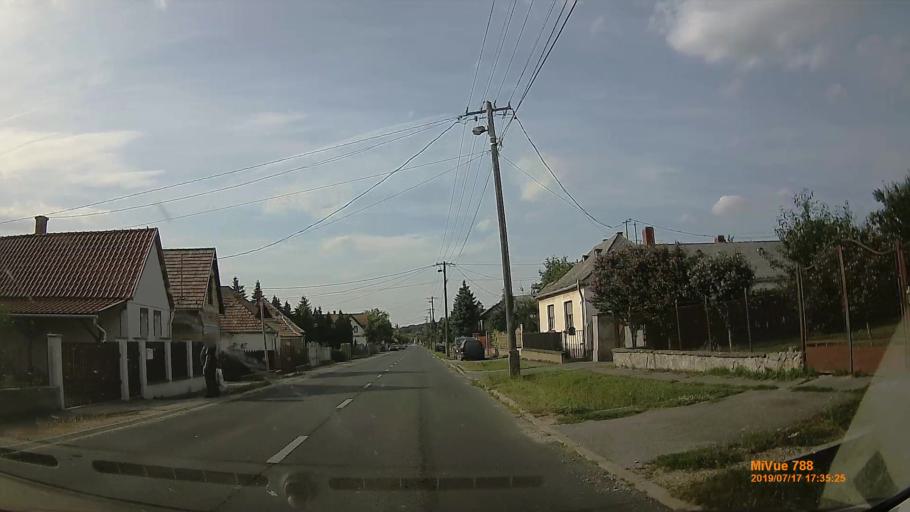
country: HU
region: Veszprem
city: Ajka
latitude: 47.0645
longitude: 17.5525
